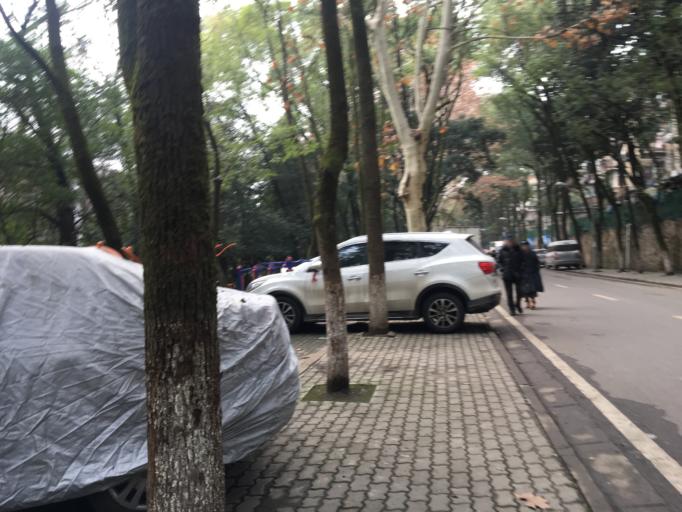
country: CN
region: Hubei
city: Guanshan
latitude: 30.5347
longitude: 114.3656
